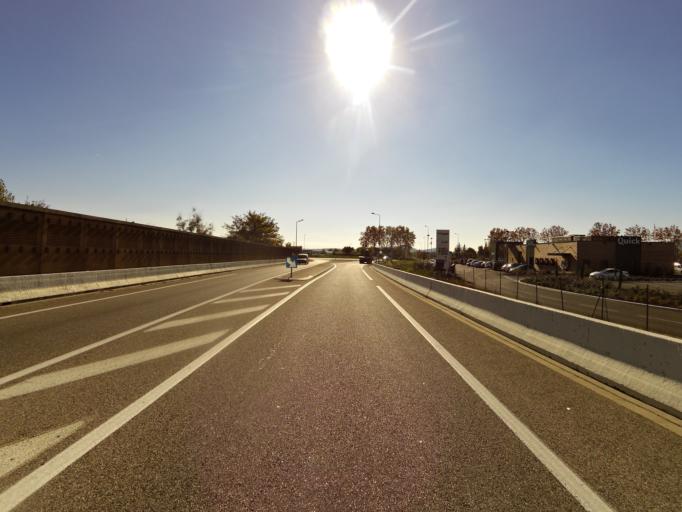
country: FR
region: Rhone-Alpes
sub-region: Departement de l'Ardeche
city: Saint-Privat
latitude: 44.6143
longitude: 4.4085
